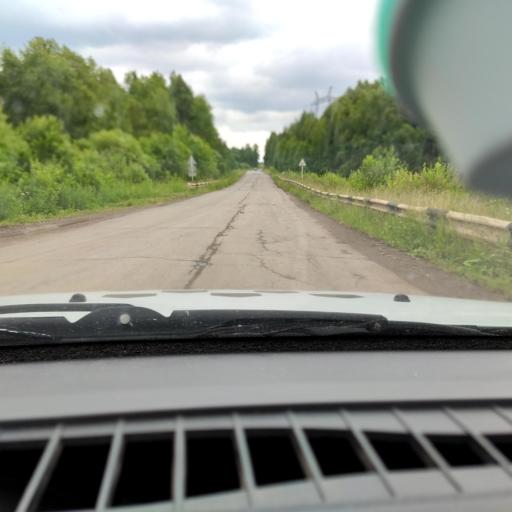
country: RU
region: Perm
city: Uinskoye
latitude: 57.1547
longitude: 56.5717
